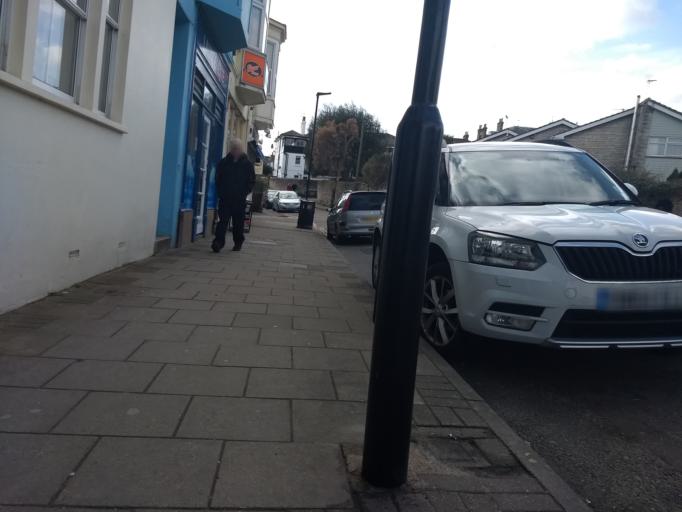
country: GB
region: England
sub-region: Isle of Wight
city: Ryde
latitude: 50.7301
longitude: -1.1542
